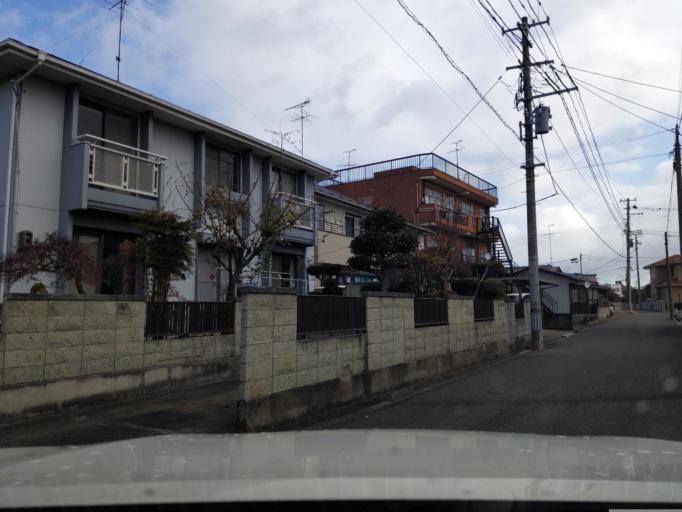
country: JP
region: Fukushima
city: Koriyama
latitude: 37.3767
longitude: 140.3629
